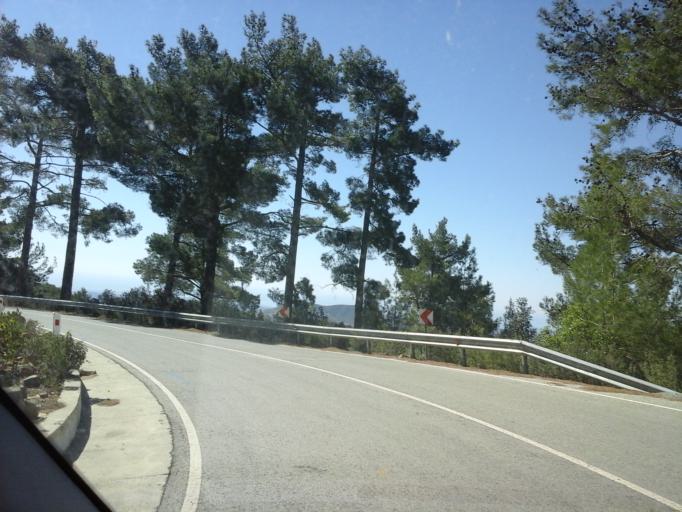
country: CY
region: Lefkosia
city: Kakopetria
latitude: 34.9115
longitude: 32.8323
